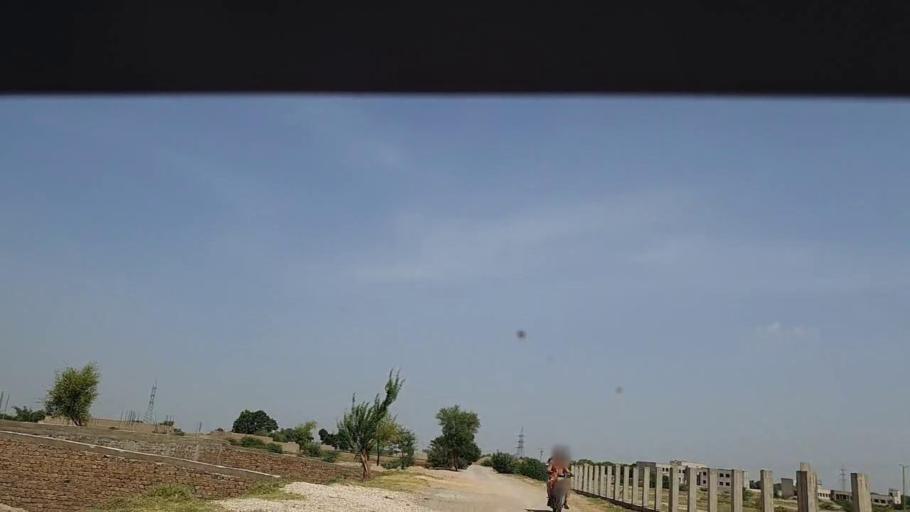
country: PK
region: Sindh
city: Phulji
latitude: 26.9603
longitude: 67.6980
